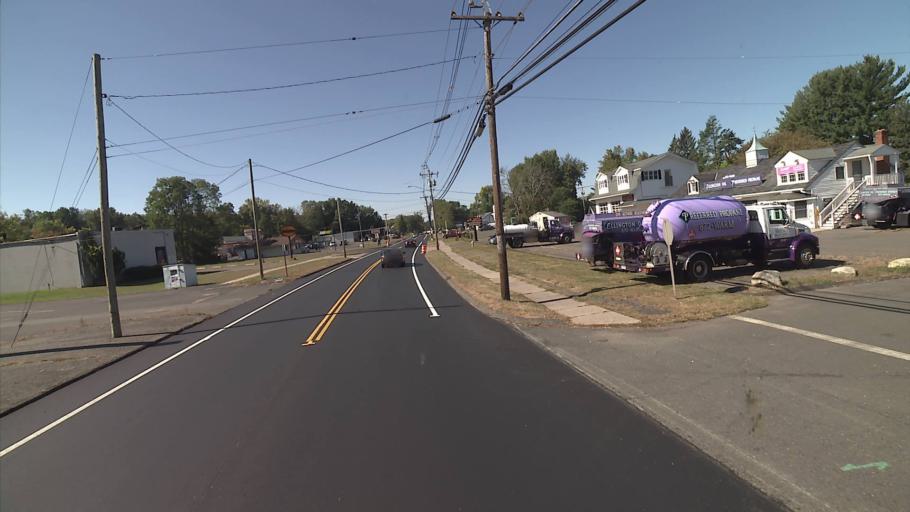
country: US
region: Connecticut
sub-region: Tolland County
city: Rockville
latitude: 41.8655
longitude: -72.4721
